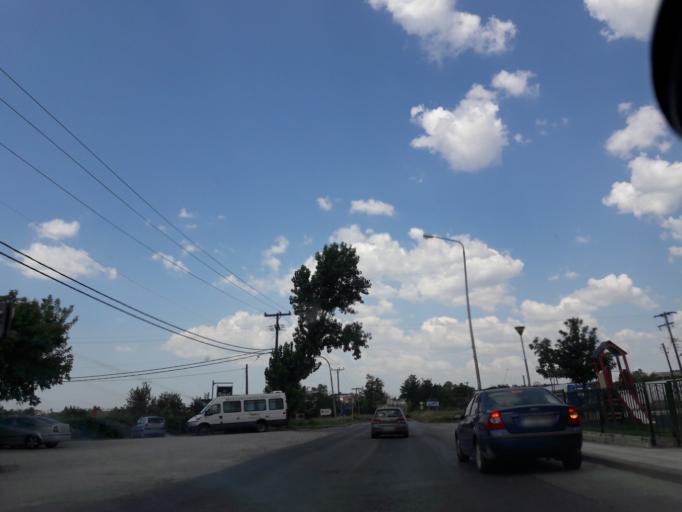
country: GR
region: Central Macedonia
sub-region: Nomos Thessalonikis
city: Thermi
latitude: 40.5261
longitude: 23.0480
